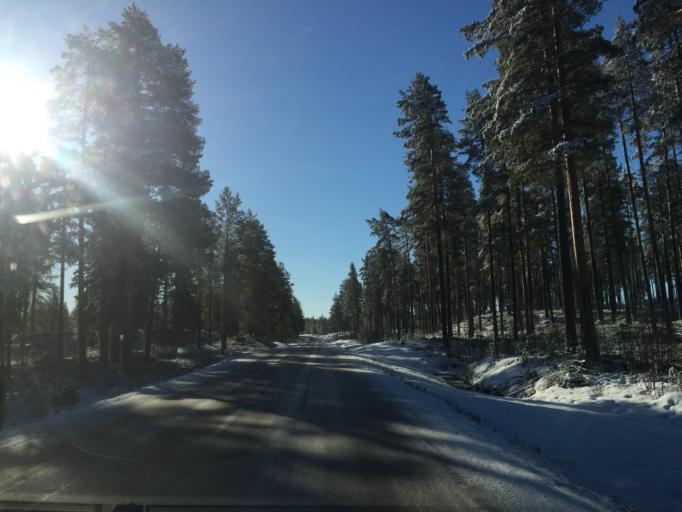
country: SE
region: Dalarna
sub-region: Vansbro Kommun
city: Vansbro
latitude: 60.8189
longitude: 14.1314
